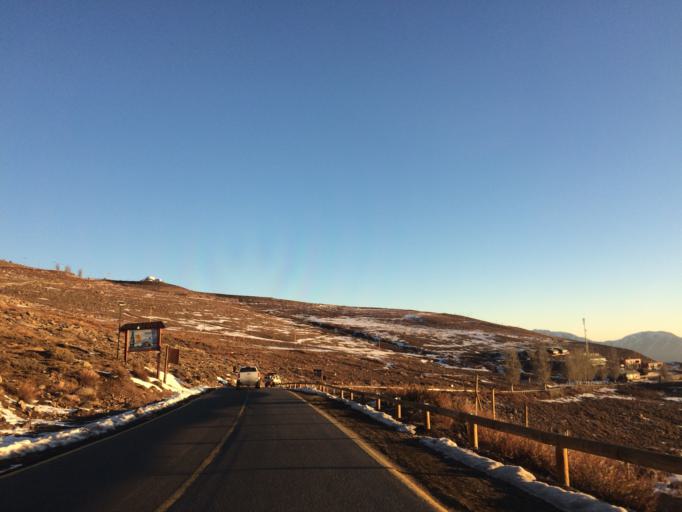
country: CL
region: Santiago Metropolitan
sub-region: Provincia de Santiago
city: Villa Presidente Frei, Nunoa, Santiago, Chile
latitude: -33.3421
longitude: -70.2960
